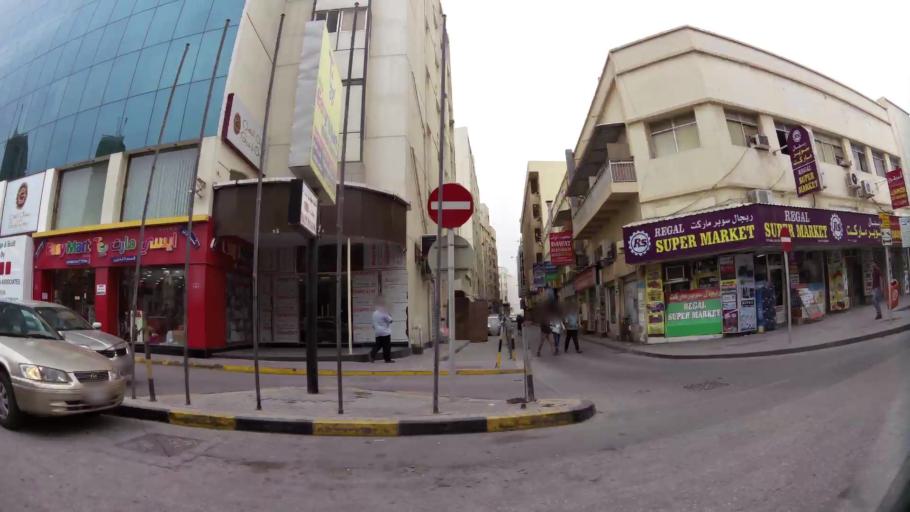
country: BH
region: Manama
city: Manama
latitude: 26.2324
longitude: 50.5724
